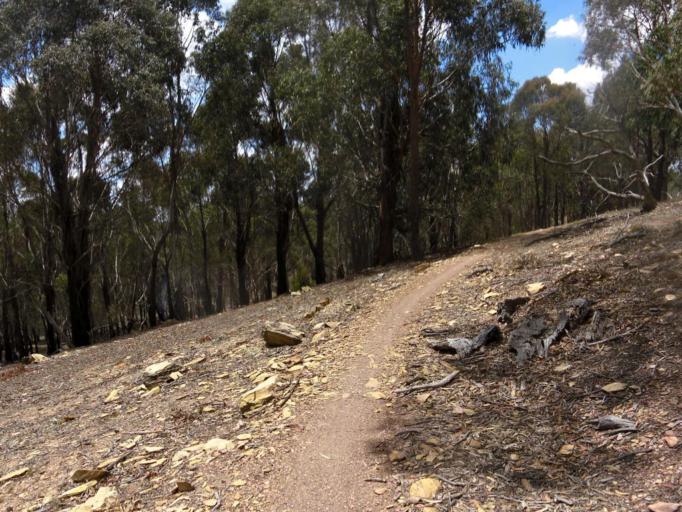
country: AU
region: Australian Capital Territory
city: Kaleen
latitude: -35.1347
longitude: 149.1367
